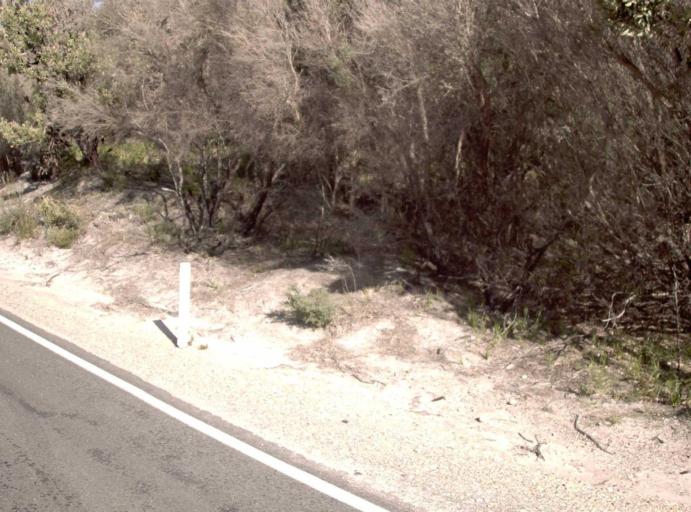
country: AU
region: Victoria
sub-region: East Gippsland
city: Lakes Entrance
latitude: -37.8004
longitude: 148.7325
